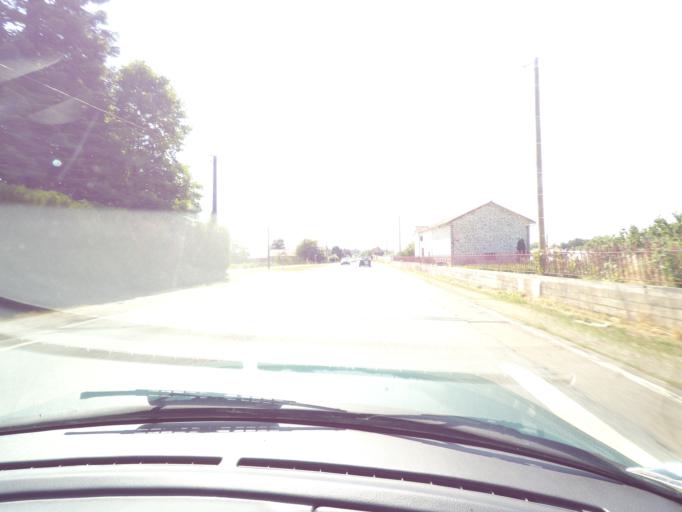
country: FR
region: Limousin
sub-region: Departement de la Haute-Vienne
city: Chaptelat
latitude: 45.9067
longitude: 1.2220
